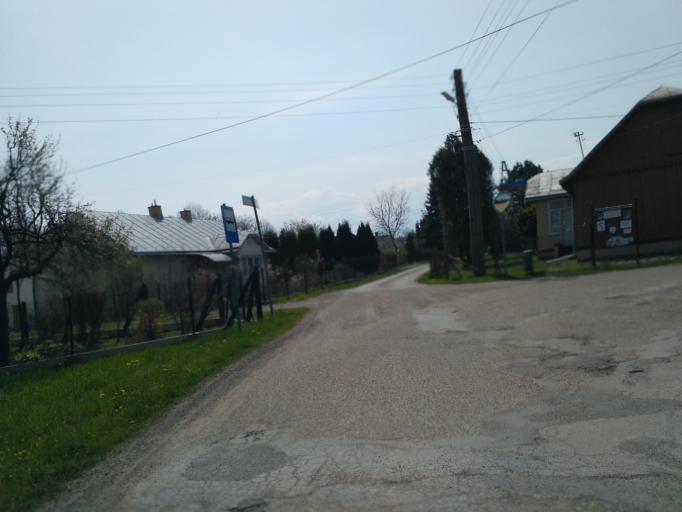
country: PL
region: Subcarpathian Voivodeship
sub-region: Powiat krosnienski
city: Miejsce Piastowe
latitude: 49.6240
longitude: 21.7314
